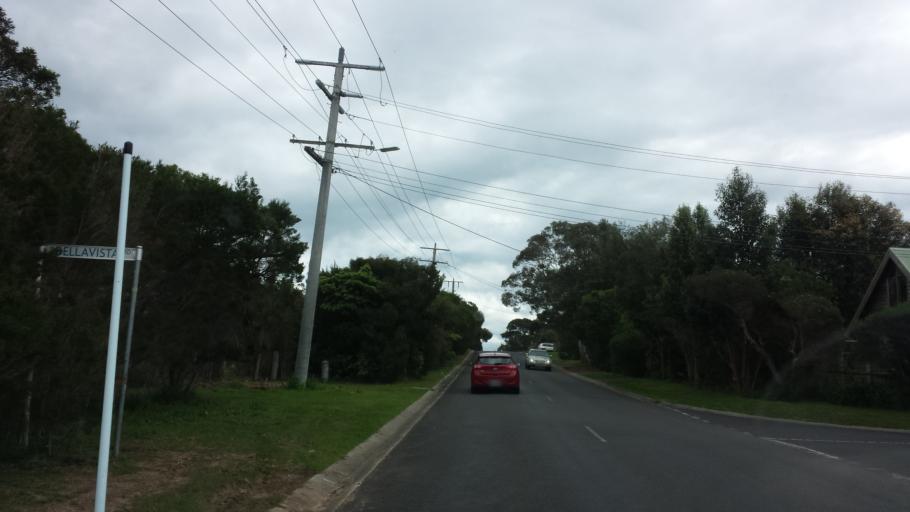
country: AU
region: Victoria
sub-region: Bass Coast
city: Cowes
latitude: -38.4523
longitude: 145.2158
